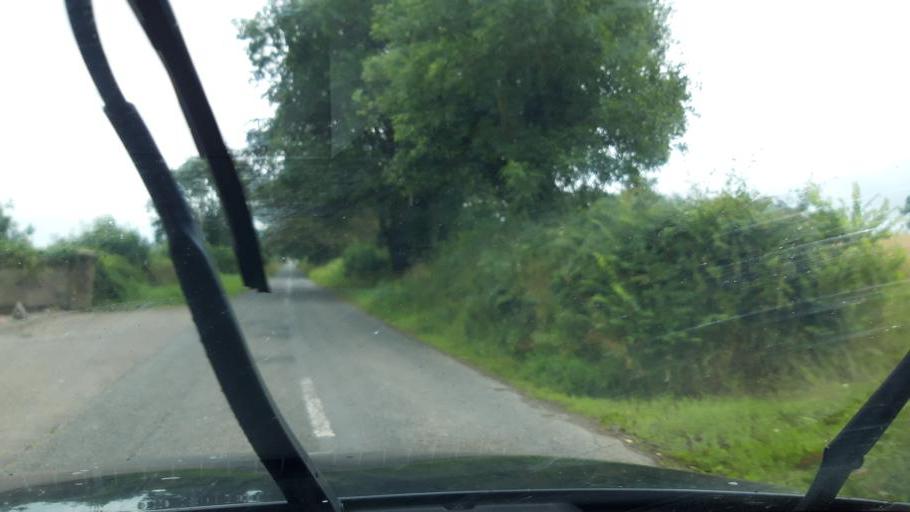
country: IE
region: Munster
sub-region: County Cork
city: Castlemartyr
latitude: 52.1354
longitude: -8.0269
